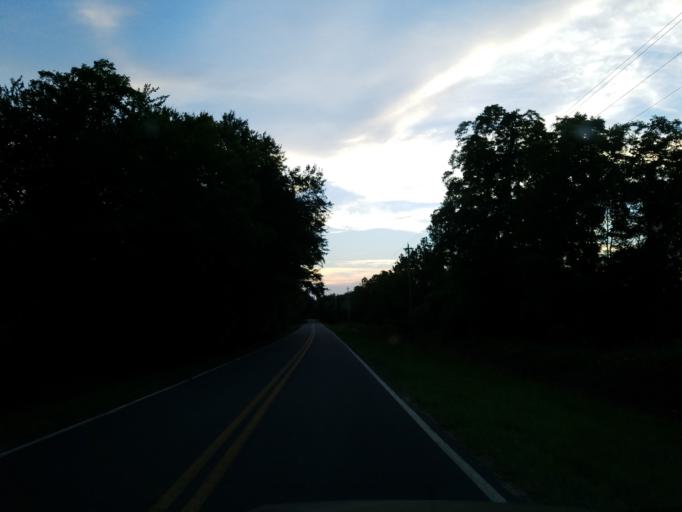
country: US
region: Georgia
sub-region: Crisp County
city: Cordele
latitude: 31.8381
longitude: -83.7458
